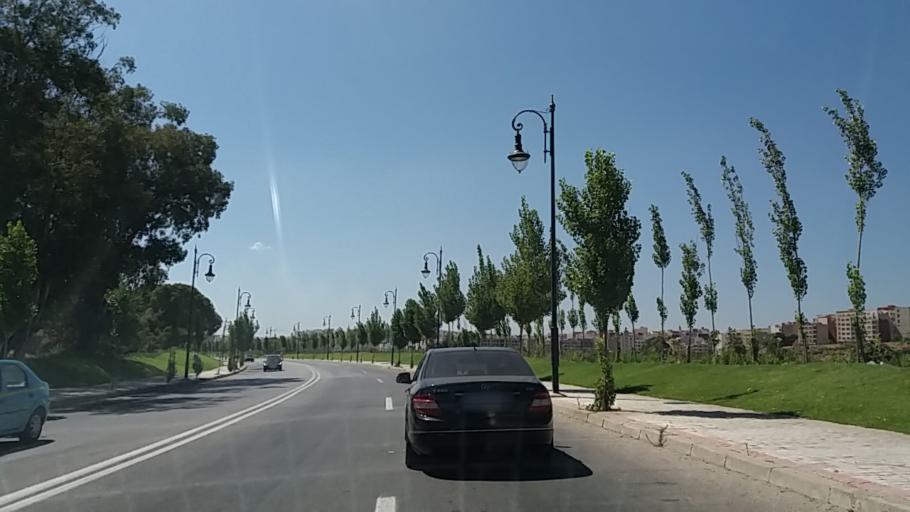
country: MA
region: Tanger-Tetouan
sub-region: Tanger-Assilah
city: Tangier
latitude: 35.7754
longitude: -5.7625
